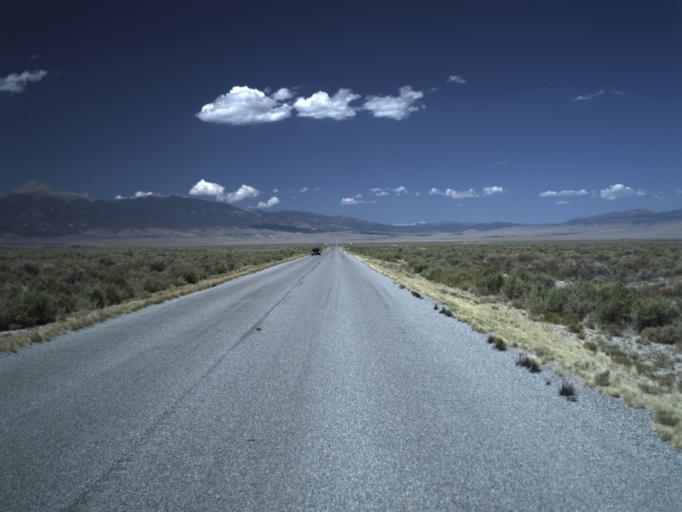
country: US
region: Nevada
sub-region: White Pine County
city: McGill
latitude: 39.0498
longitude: -113.9531
